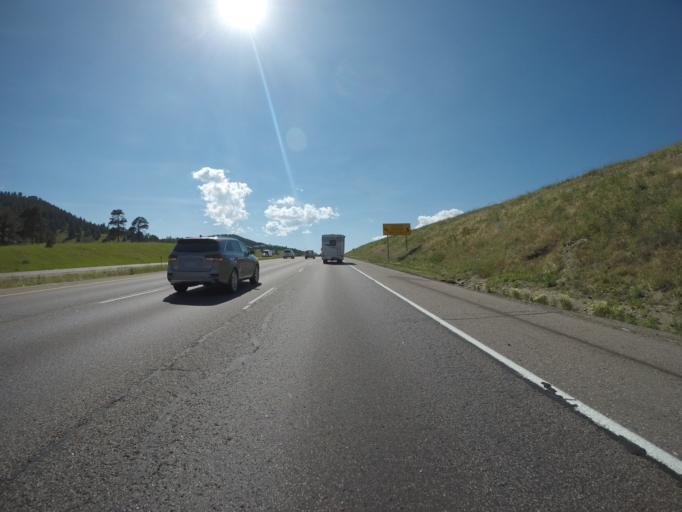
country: US
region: Colorado
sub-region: Jefferson County
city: Genesee
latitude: 39.7053
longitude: -105.2709
